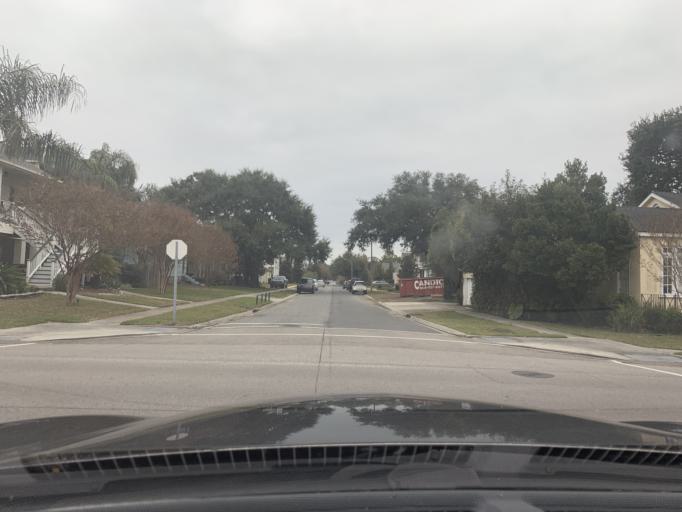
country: US
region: Louisiana
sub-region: Jefferson Parish
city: Metairie
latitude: 30.0123
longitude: -90.1084
